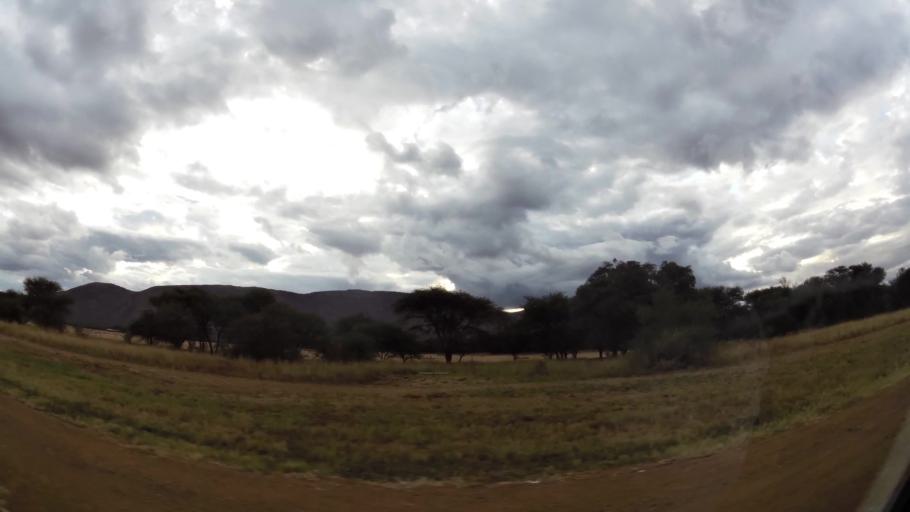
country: ZA
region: Limpopo
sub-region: Waterberg District Municipality
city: Mokopane
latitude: -24.2417
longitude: 28.9944
